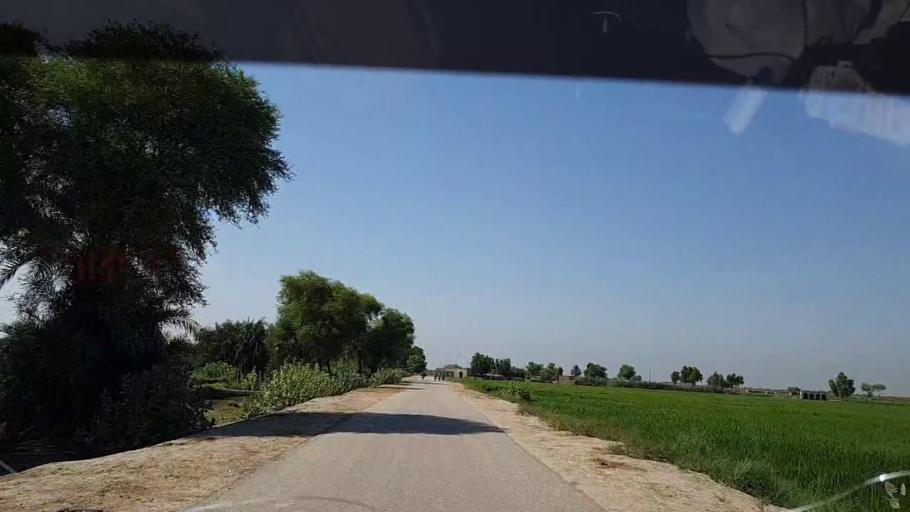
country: PK
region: Sindh
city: Kandhkot
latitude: 28.3064
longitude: 69.1099
